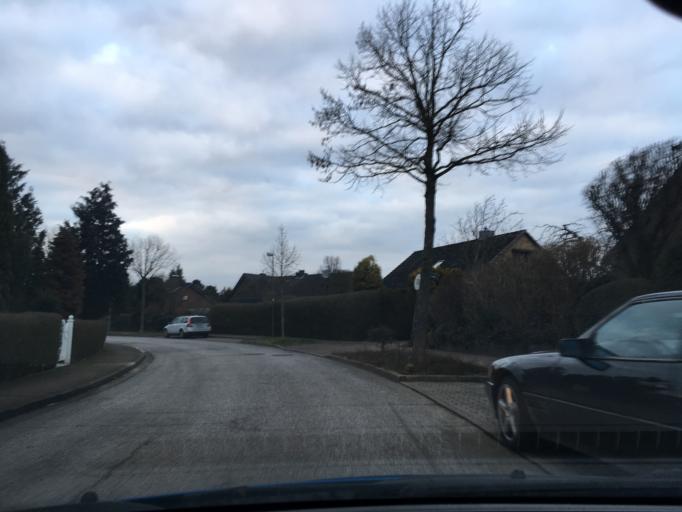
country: DE
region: Schleswig-Holstein
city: Wedel
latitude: 53.5902
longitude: 9.6957
